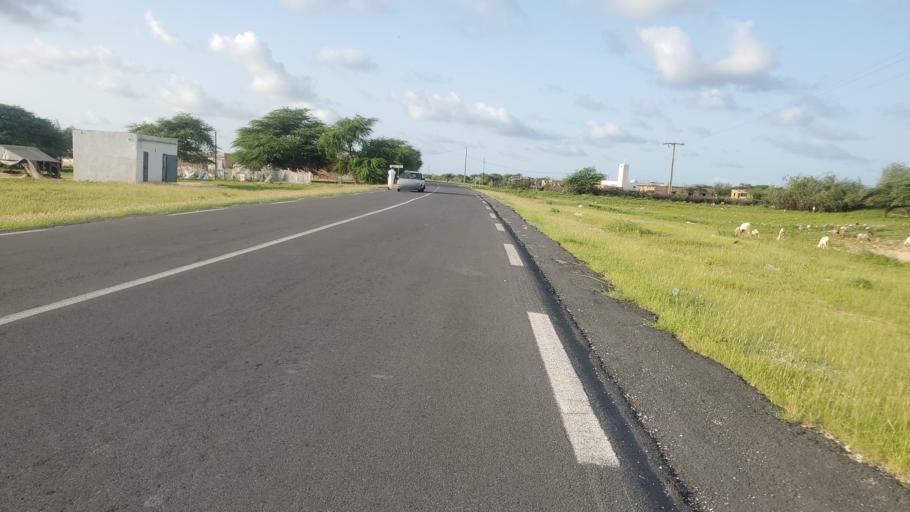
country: SN
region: Saint-Louis
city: Saint-Louis
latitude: 16.1399
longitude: -16.4099
